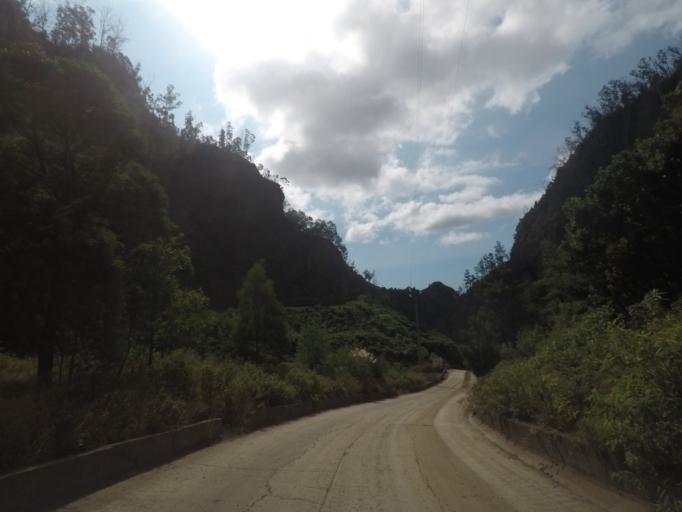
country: PT
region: Madeira
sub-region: Funchal
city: Nossa Senhora do Monte
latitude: 32.6869
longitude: -16.9152
